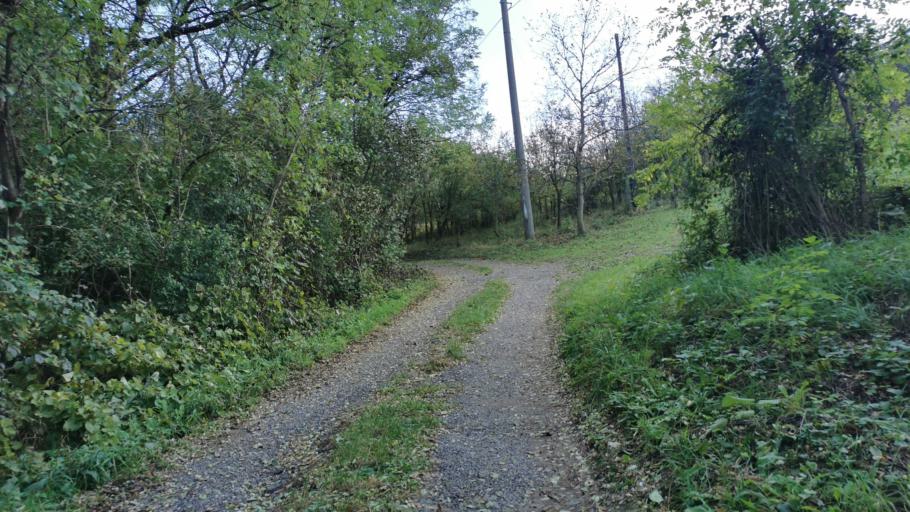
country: SK
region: Trnavsky
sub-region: Okres Skalica
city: Skalica
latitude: 48.8204
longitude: 17.2329
